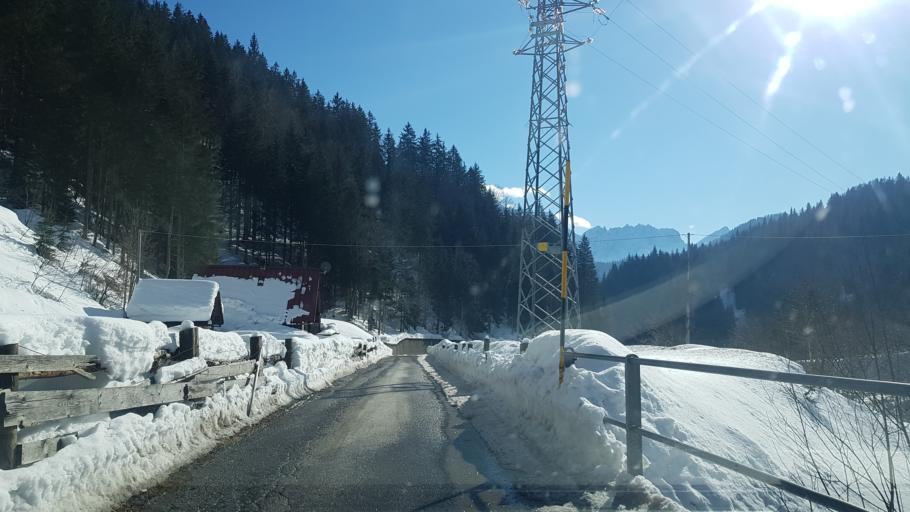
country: IT
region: Friuli Venezia Giulia
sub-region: Provincia di Udine
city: Malborghetto
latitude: 46.5429
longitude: 13.4752
